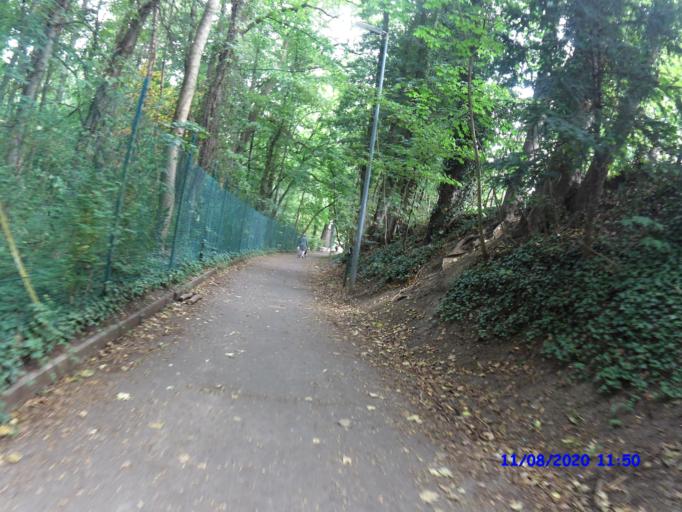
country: BE
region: Brussels Capital
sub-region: Bruxelles-Capitale
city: Brussels
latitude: 50.8088
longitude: 4.3511
